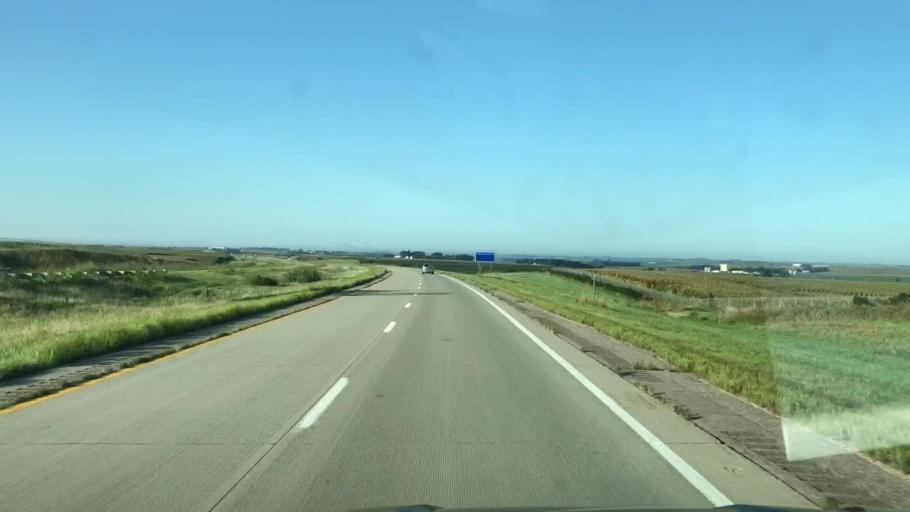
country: US
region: Iowa
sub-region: Plymouth County
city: Le Mars
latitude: 42.8095
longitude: -96.1969
